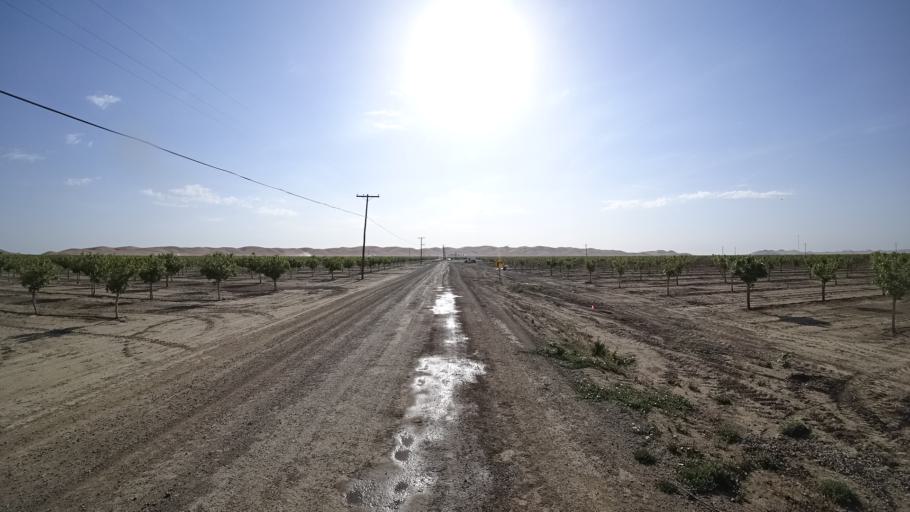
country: US
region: California
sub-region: Kings County
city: Avenal
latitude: 35.8180
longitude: -120.0609
